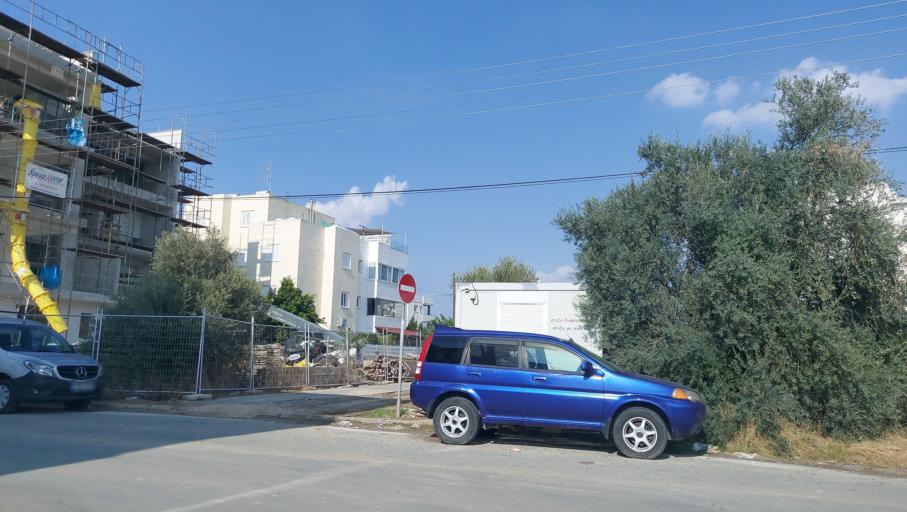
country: CY
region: Lefkosia
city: Tseri
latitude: 35.1078
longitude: 33.3067
